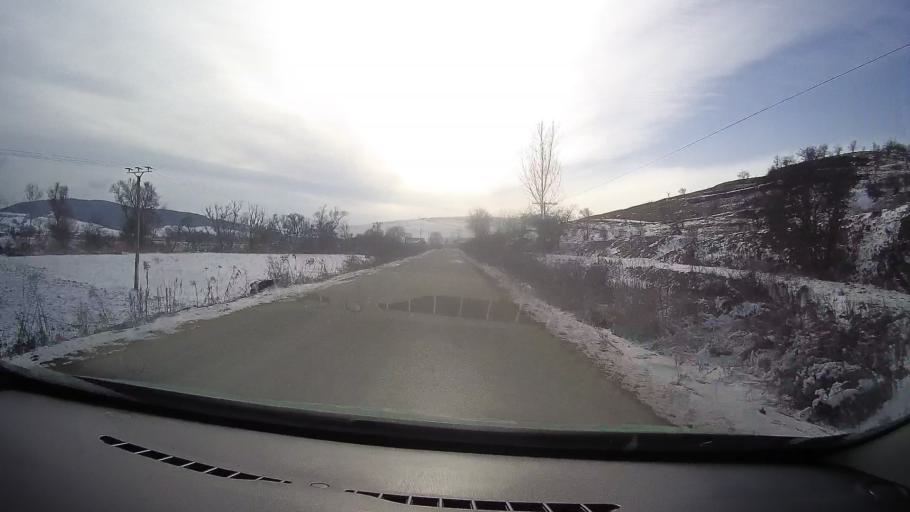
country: RO
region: Sibiu
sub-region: Oras Agnita
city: Ruja
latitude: 46.0045
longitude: 24.6760
